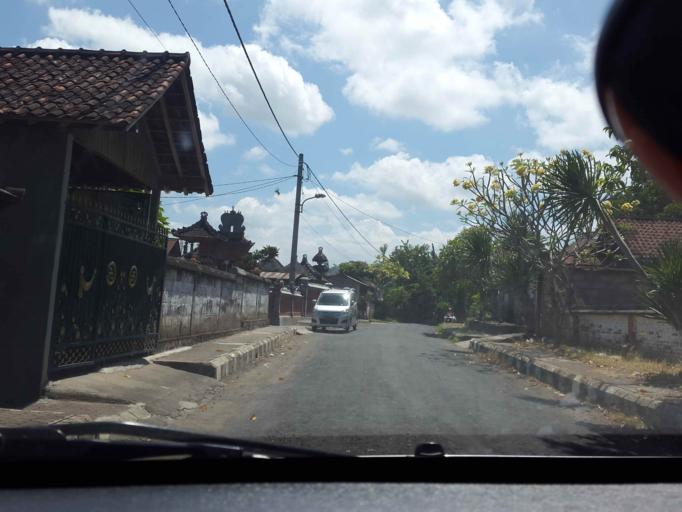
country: ID
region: Bali
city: Klungkung
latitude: -8.5225
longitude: 115.3963
